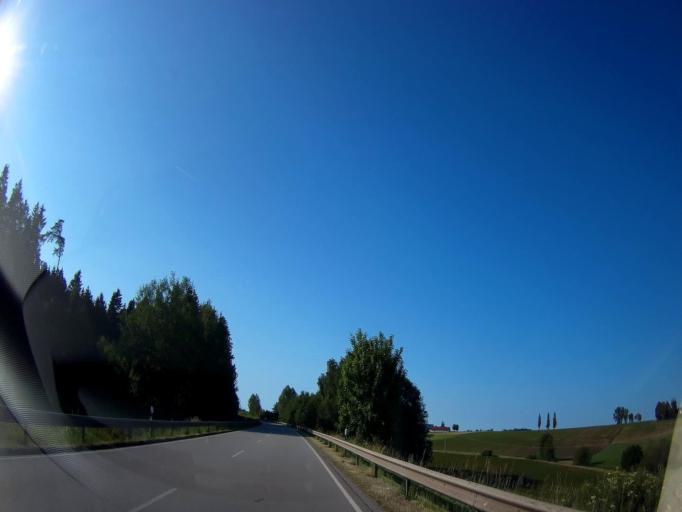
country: DE
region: Bavaria
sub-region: Lower Bavaria
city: Falkenberg
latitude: 48.4443
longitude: 12.7387
